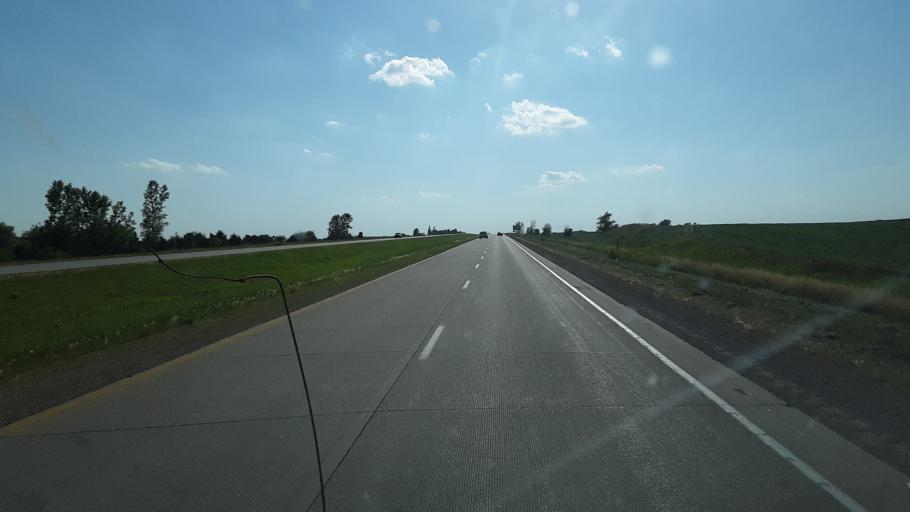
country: US
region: Iowa
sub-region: Grundy County
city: Dike
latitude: 42.4631
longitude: -92.7339
